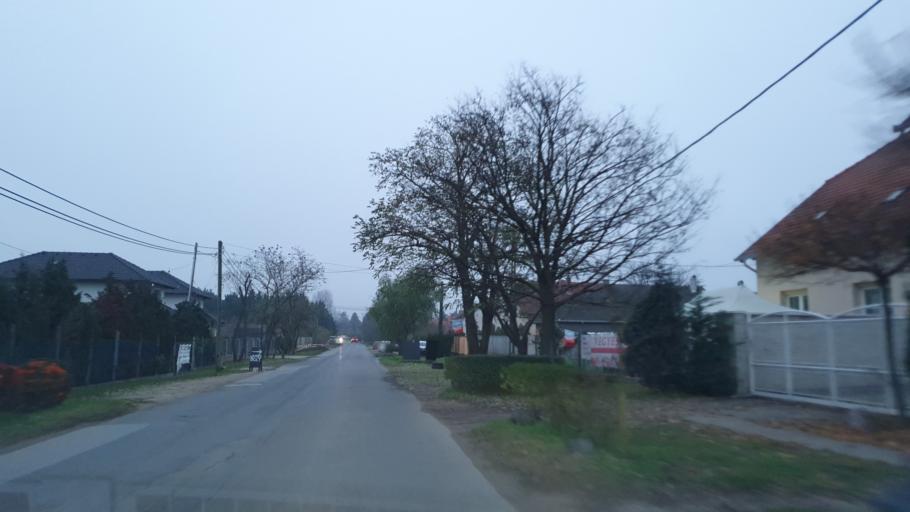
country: HU
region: Pest
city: Csomor
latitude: 47.5310
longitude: 19.2226
